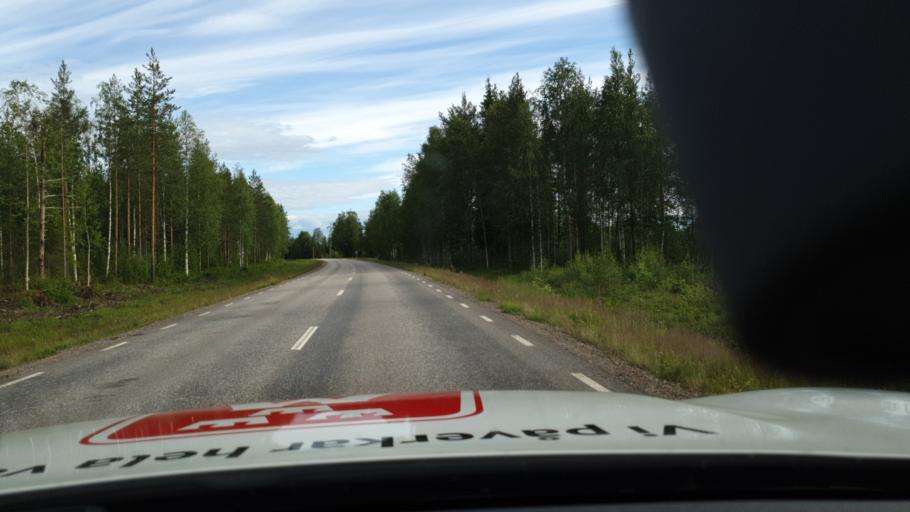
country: SE
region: Norrbotten
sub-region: Overkalix Kommun
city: OEverkalix
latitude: 66.5061
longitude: 22.7645
